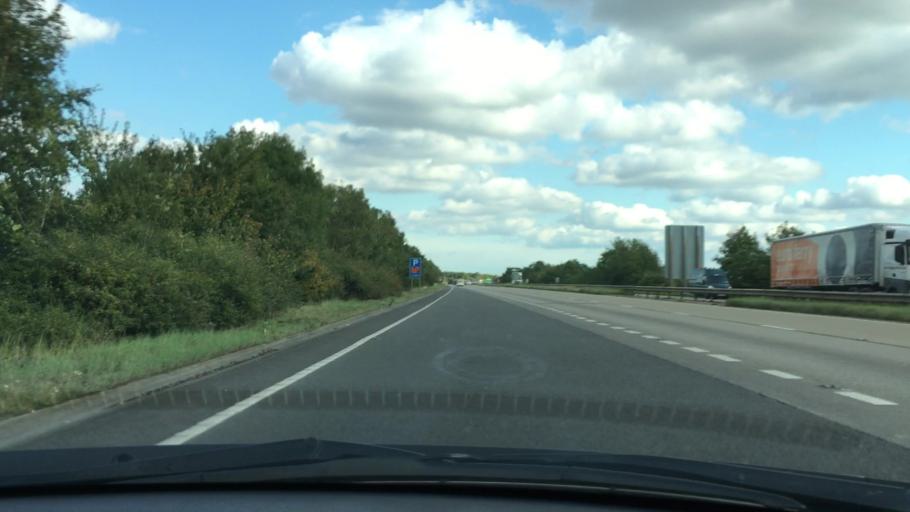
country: GB
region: England
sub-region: North East Lincolnshire
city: Healing
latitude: 53.5968
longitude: -0.1904
